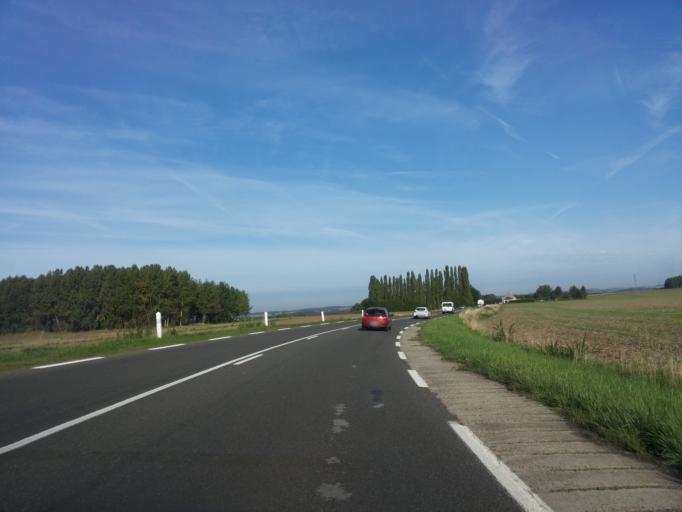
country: FR
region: Picardie
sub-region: Departement de l'Aisne
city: Charmes
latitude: 49.6383
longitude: 3.4022
